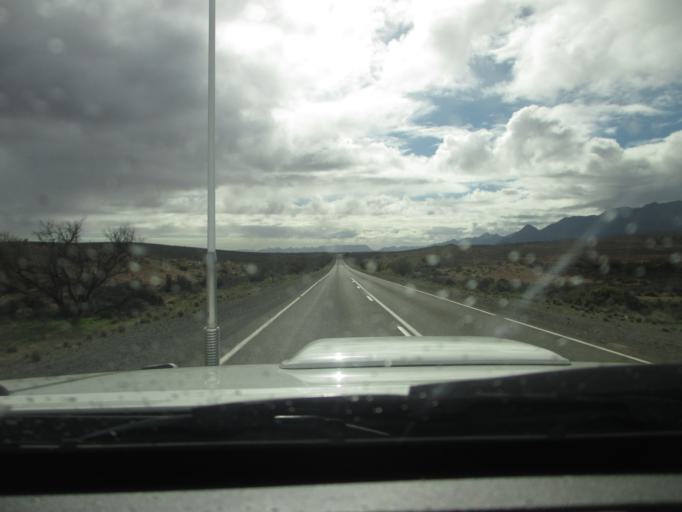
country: AU
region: South Australia
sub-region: Flinders Ranges
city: Quorn
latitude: -31.5827
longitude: 138.4176
